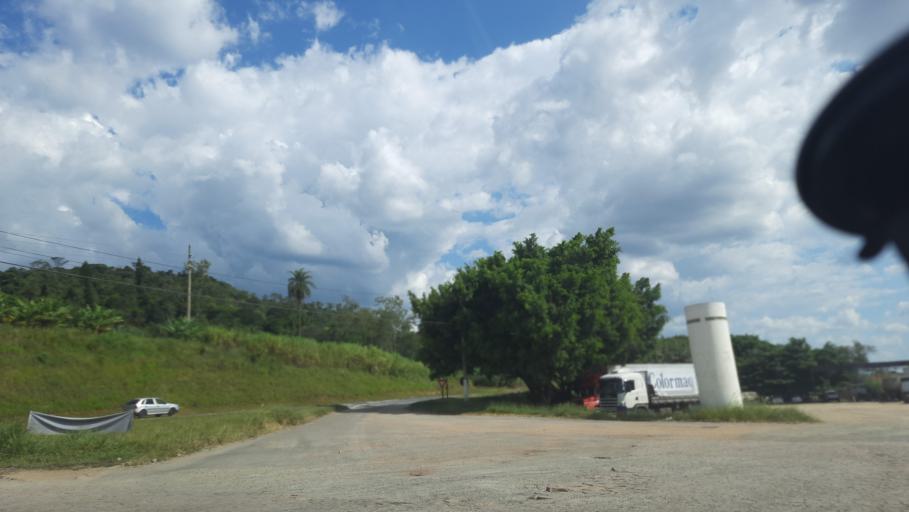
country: BR
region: Sao Paulo
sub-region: Sao Jose Do Rio Pardo
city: Sao Jose do Rio Pardo
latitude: -21.6369
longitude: -46.9049
